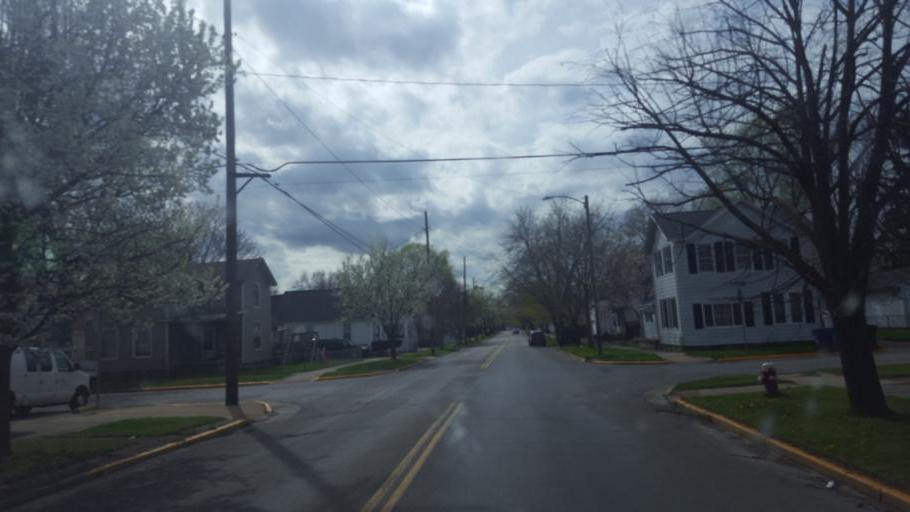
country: US
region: Ohio
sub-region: Erie County
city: Sandusky
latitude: 41.4466
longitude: -82.7229
